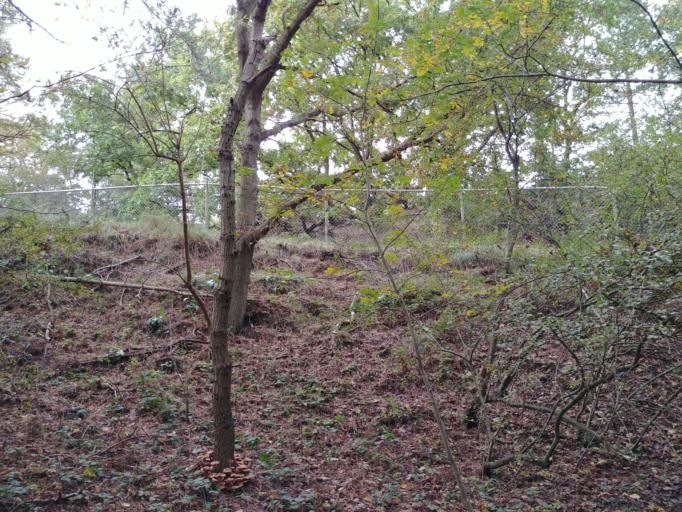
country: NL
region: North Holland
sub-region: Gemeente Zandvoort
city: Zandvoort
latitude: 52.3803
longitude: 4.5780
